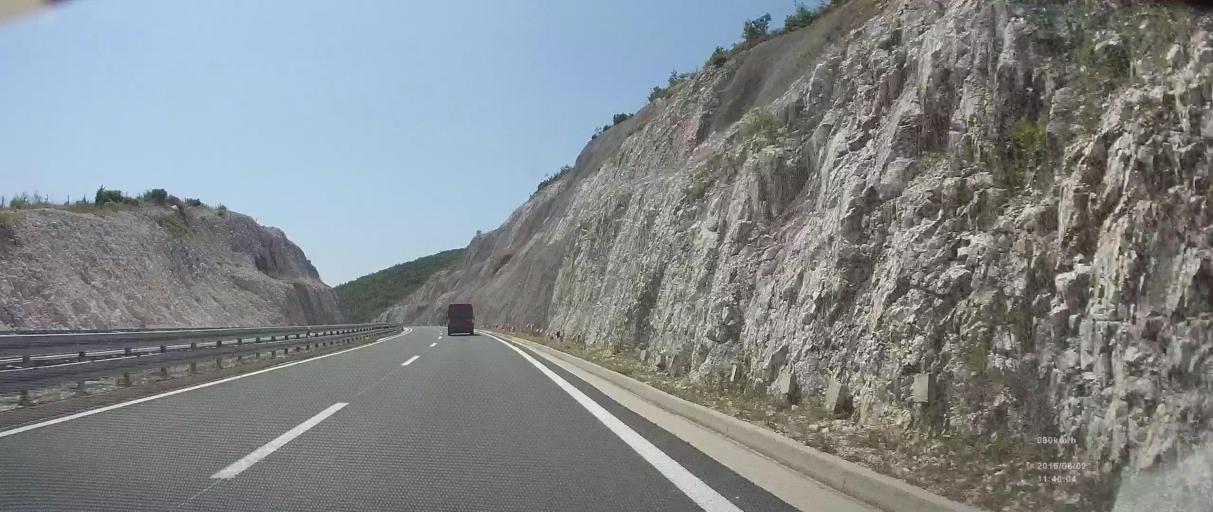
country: HR
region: Dubrovacko-Neretvanska
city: Komin
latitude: 43.0792
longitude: 17.4895
